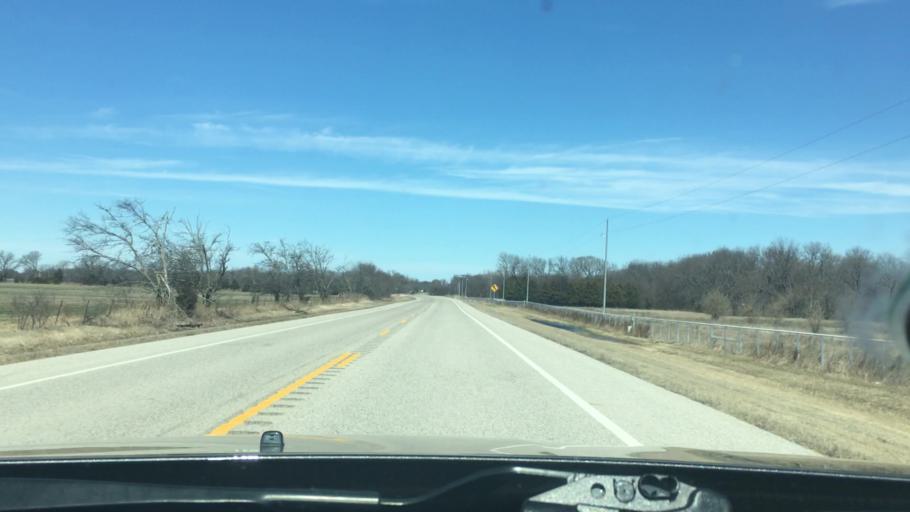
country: US
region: Oklahoma
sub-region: Murray County
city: Sulphur
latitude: 34.3833
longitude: -96.9508
